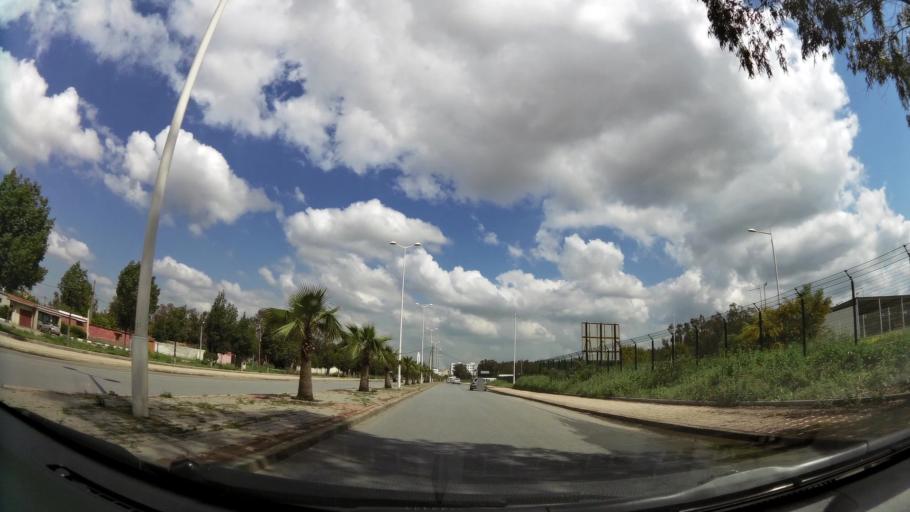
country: MA
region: Chaouia-Ouardigha
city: Nouaseur
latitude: 33.3725
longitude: -7.5476
